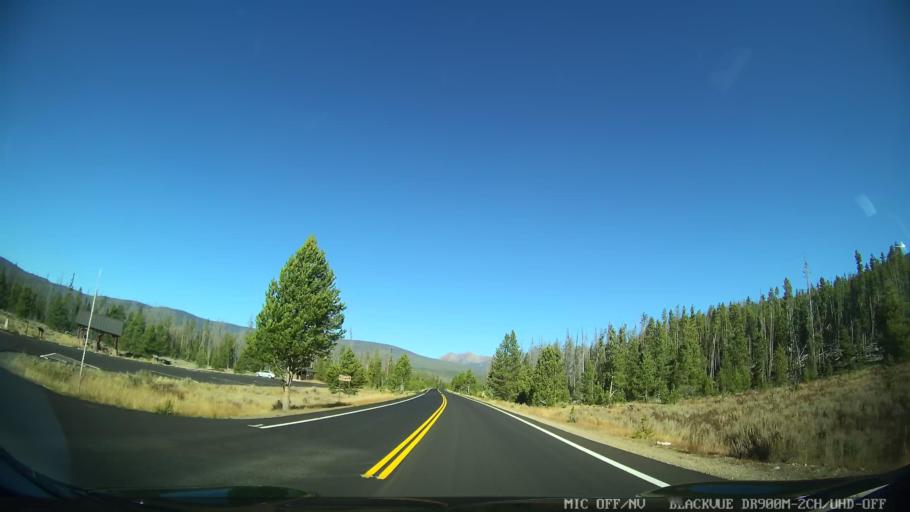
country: US
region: Colorado
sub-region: Grand County
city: Granby
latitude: 40.2816
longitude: -105.8372
